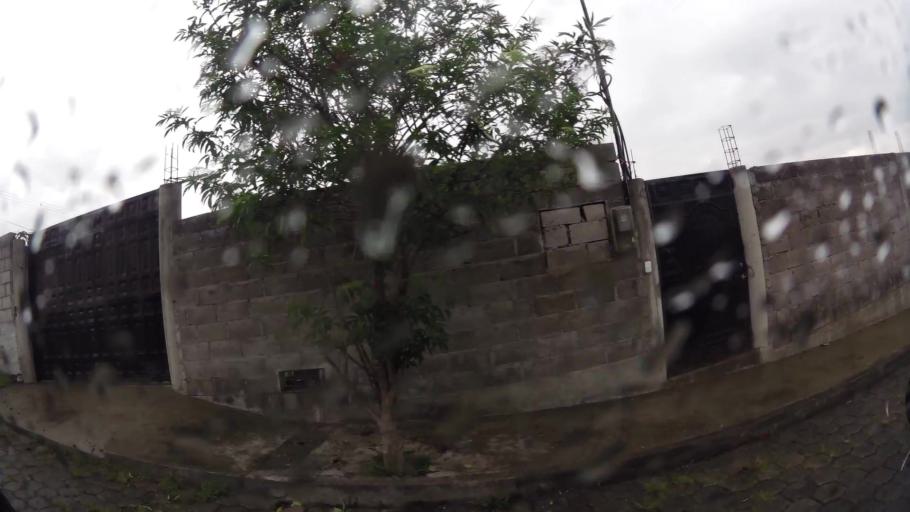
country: EC
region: Pichincha
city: Sangolqui
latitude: -0.3197
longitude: -78.4336
